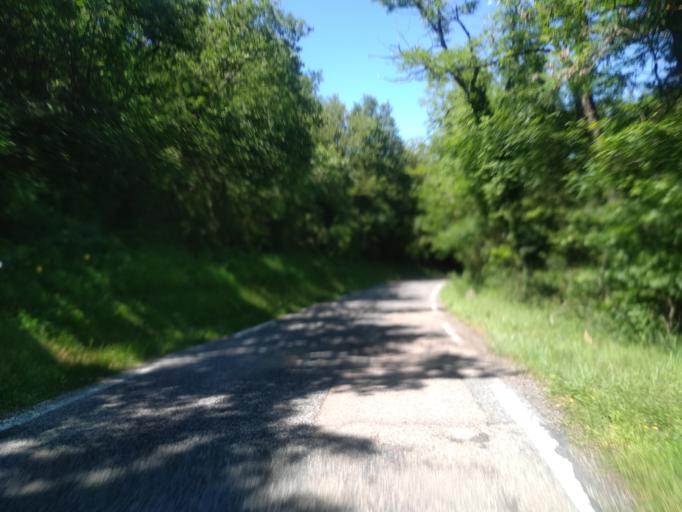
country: FR
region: Rhone-Alpes
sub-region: Departement du Rhone
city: Albigny-sur-Saone
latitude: 45.8503
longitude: 4.8131
